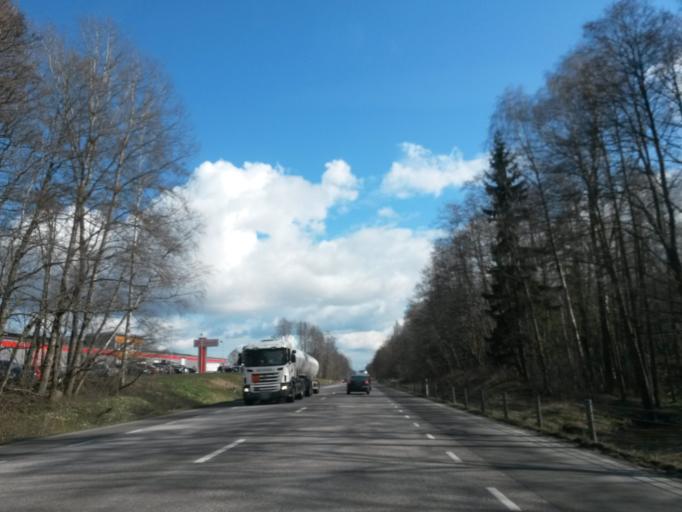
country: SE
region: Vaestra Goetaland
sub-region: Skovde Kommun
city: Skoevde
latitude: 58.3881
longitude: 13.7941
